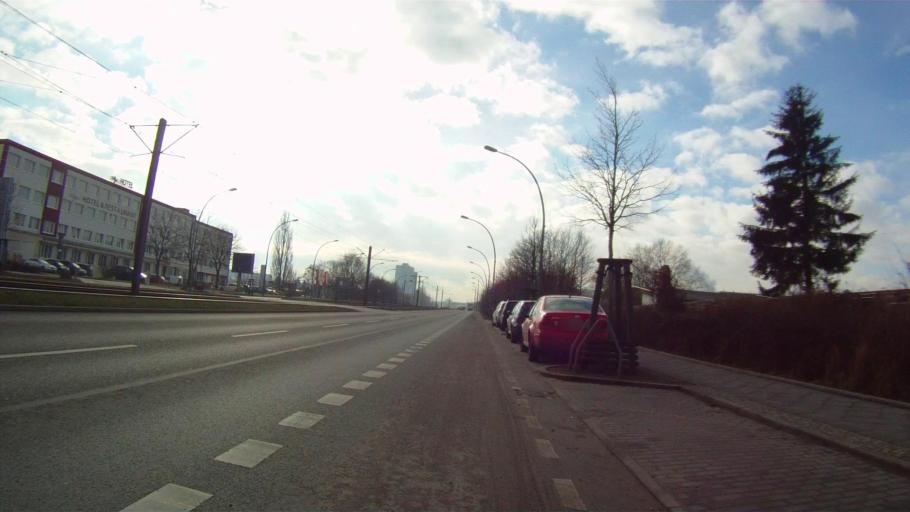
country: DE
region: Berlin
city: Friedrichsfelde
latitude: 52.5169
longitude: 13.5190
